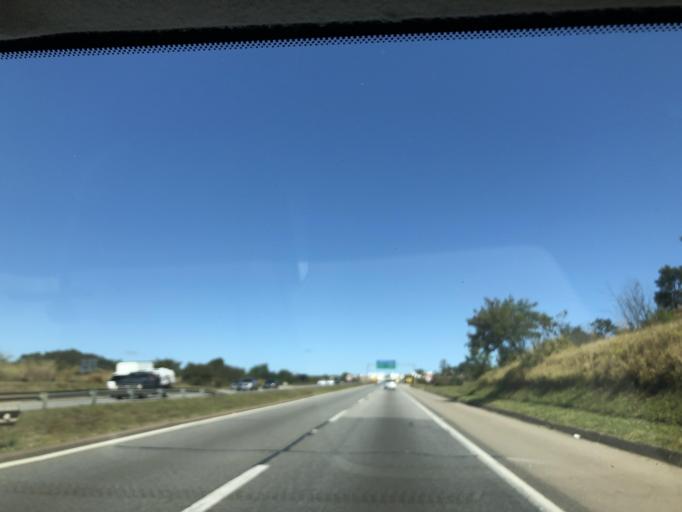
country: BR
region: Sao Paulo
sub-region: Sorocaba
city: Sorocaba
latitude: -23.4880
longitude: -47.3893
